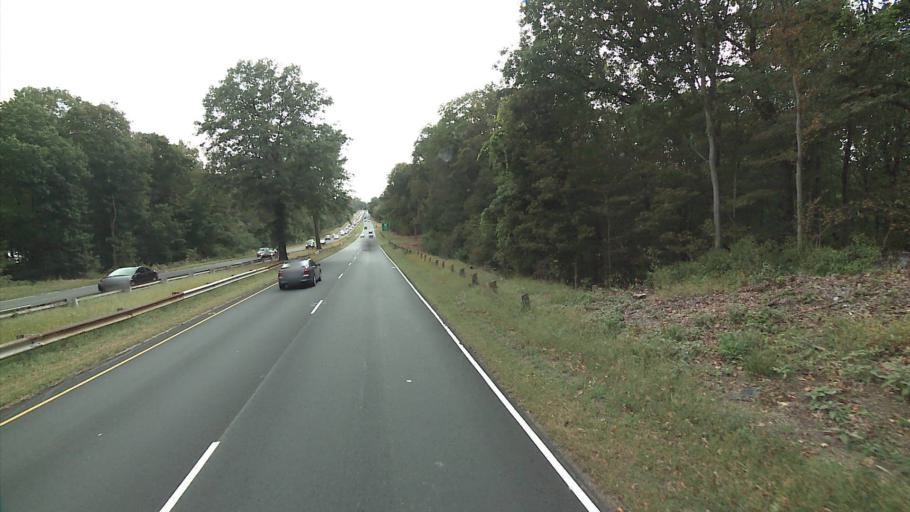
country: US
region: Connecticut
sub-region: Fairfield County
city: Westport
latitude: 41.1669
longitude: -73.3479
